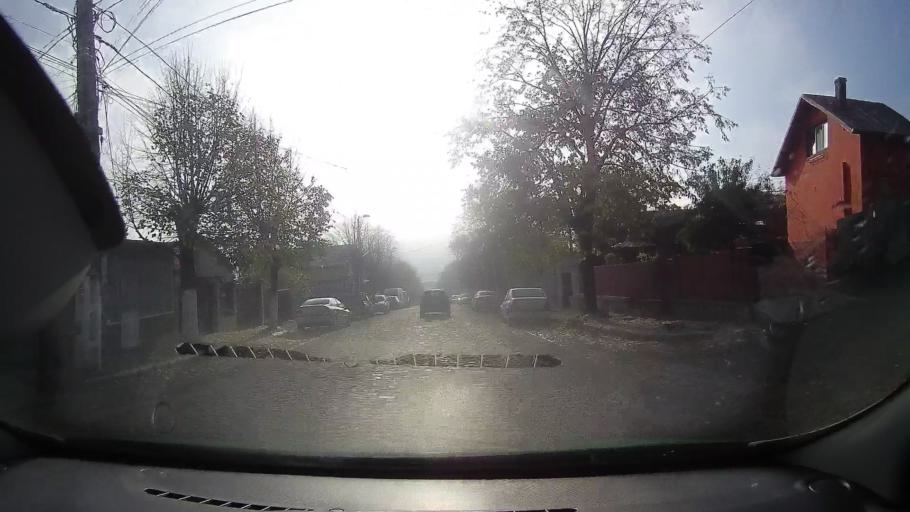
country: RO
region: Tulcea
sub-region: Municipiul Tulcea
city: Tulcea
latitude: 45.1674
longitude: 28.8151
